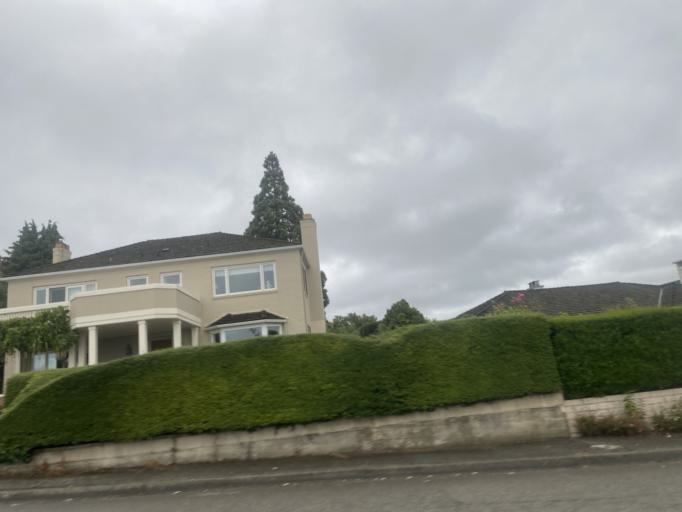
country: US
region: Washington
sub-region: King County
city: Seattle
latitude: 47.6352
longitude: -122.4045
